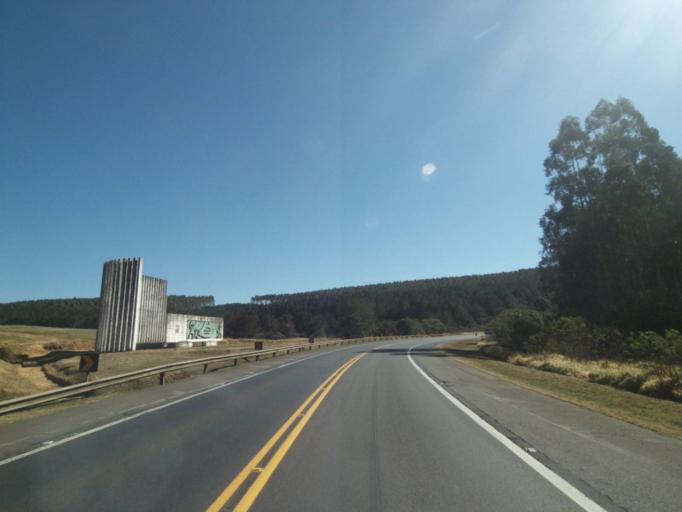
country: BR
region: Parana
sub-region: Tibagi
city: Tibagi
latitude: -24.6978
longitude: -50.5817
